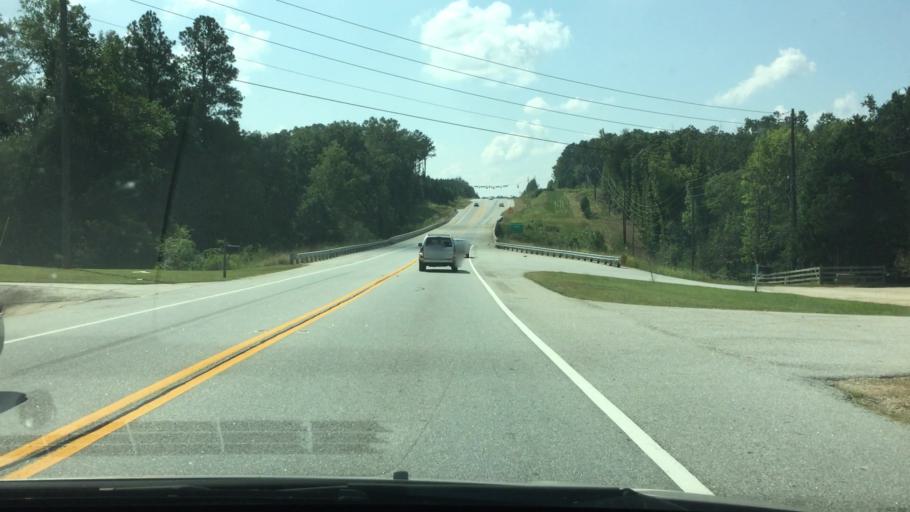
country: US
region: Georgia
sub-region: Henry County
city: McDonough
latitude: 33.5349
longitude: -84.1388
